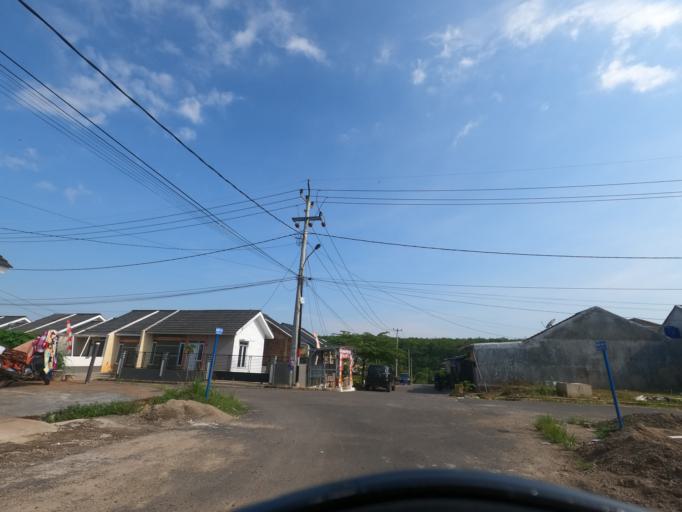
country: ID
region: West Java
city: Pamanukan
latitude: -6.5720
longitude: 107.7925
